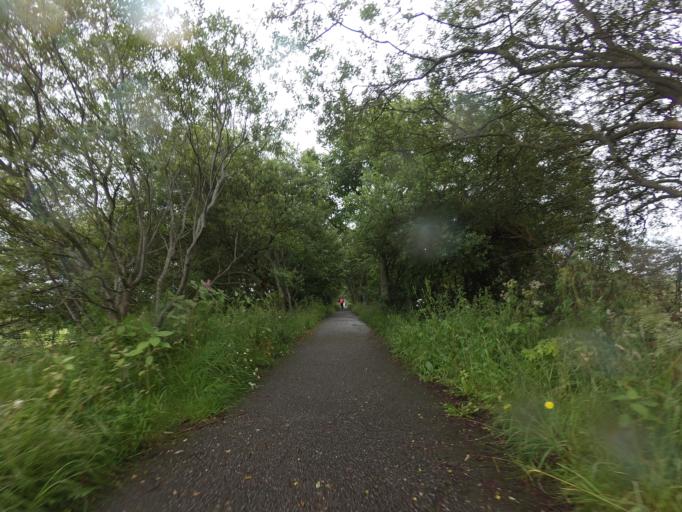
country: GB
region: Scotland
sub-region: Moray
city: Fochabers
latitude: 57.6628
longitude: -3.1031
